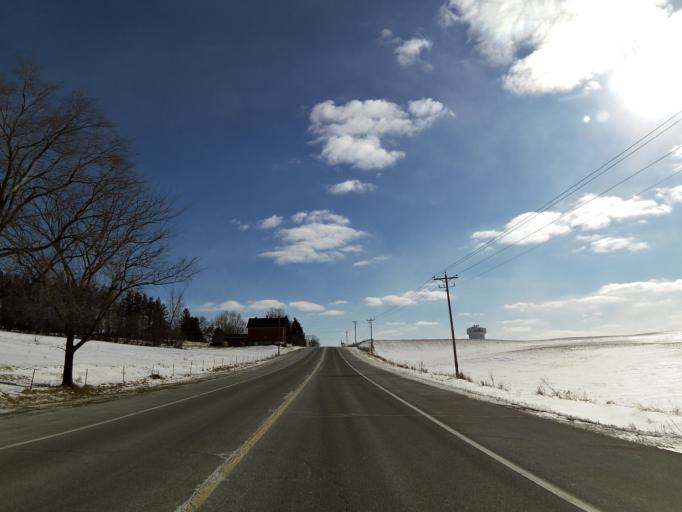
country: US
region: Minnesota
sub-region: Washington County
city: Afton
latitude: 44.9094
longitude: -92.8626
